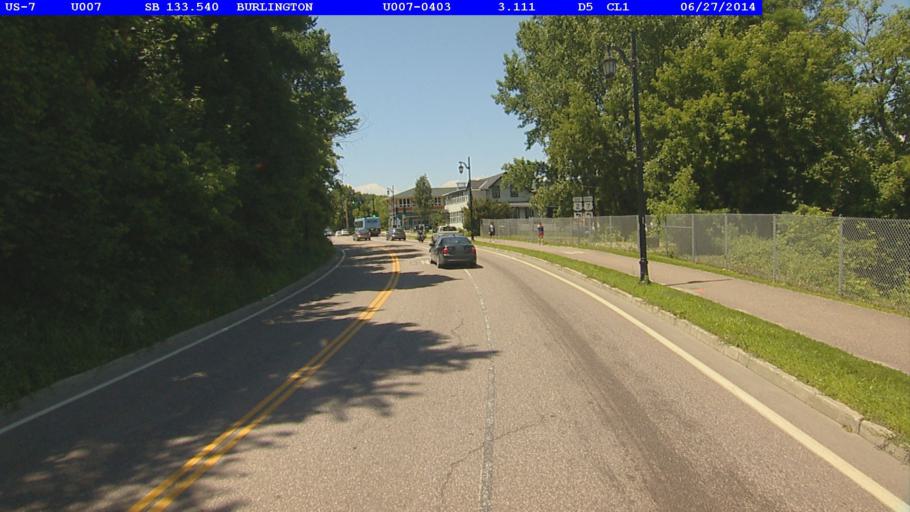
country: US
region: Vermont
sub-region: Chittenden County
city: Burlington
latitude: 44.4896
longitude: -73.2045
